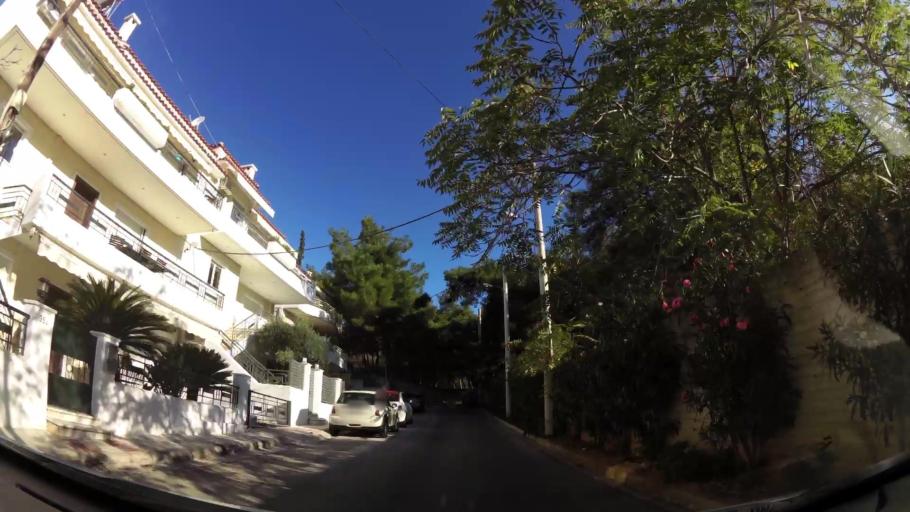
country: GR
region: Attica
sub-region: Nomarchia Athinas
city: Lykovrysi
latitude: 38.0576
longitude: 23.7820
